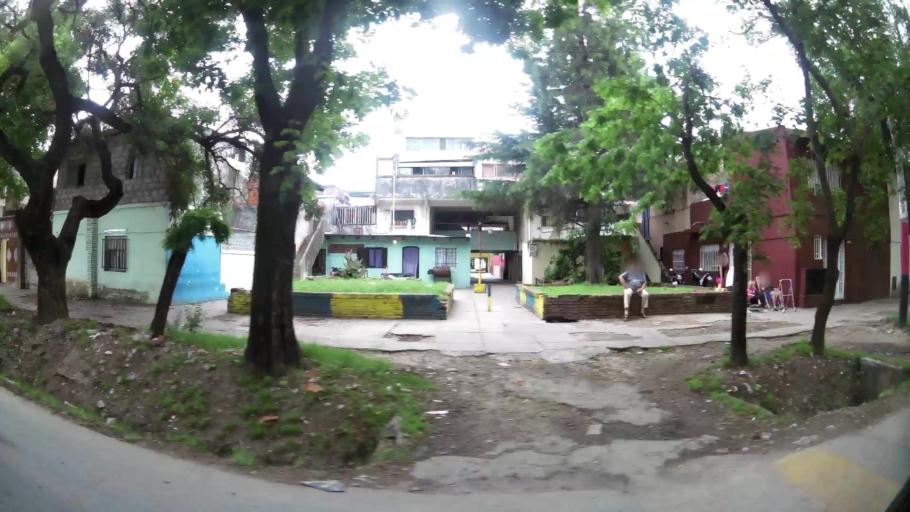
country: AR
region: Santa Fe
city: Gobernador Galvez
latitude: -32.9946
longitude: -60.6536
